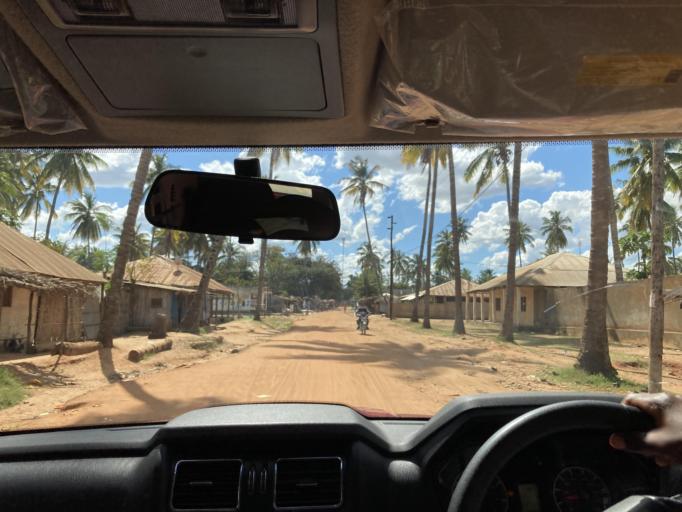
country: MZ
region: Cabo Delgado
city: Montepuez
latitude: -13.1314
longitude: 39.0058
